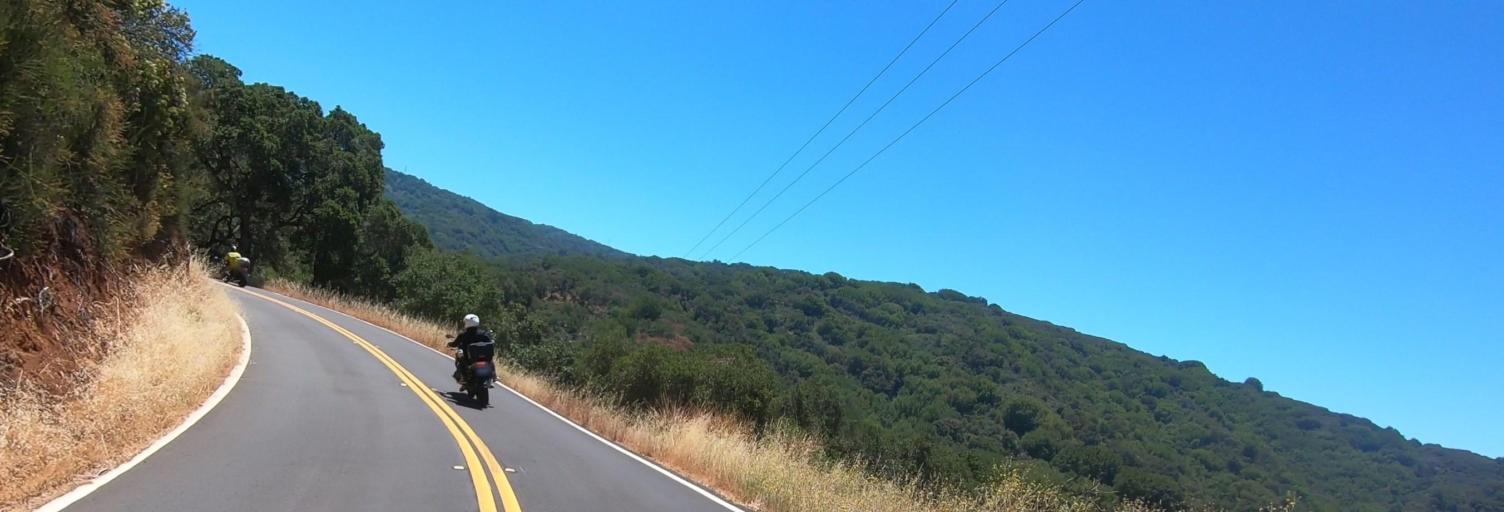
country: US
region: California
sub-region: Santa Clara County
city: Los Altos Hills
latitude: 37.3574
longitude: -122.1740
